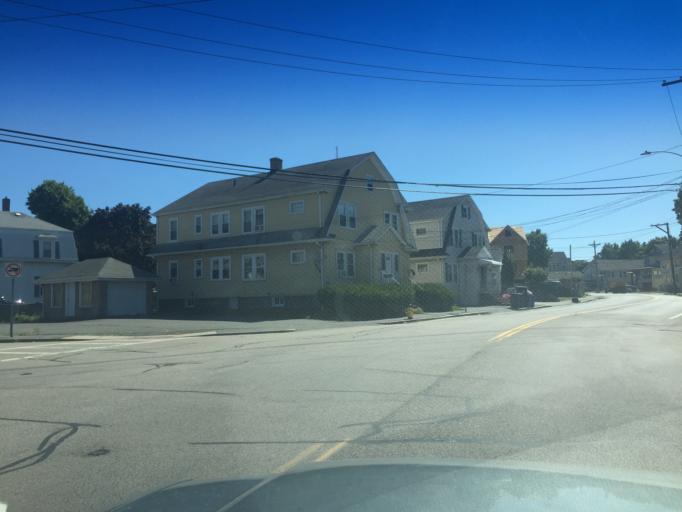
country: US
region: Massachusetts
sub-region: Norfolk County
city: Quincy
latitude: 42.2443
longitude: -70.9919
